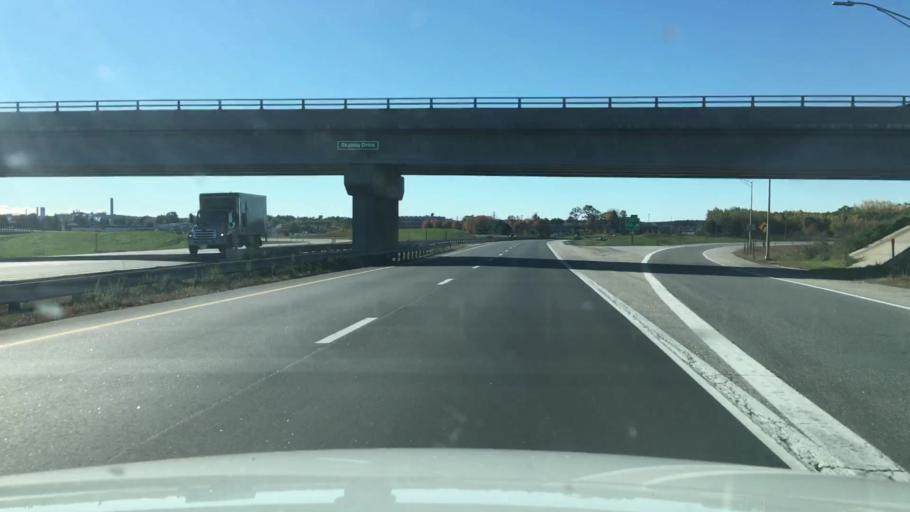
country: US
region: Maine
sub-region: Cumberland County
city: South Portland Gardens
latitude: 43.6499
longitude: -70.3314
